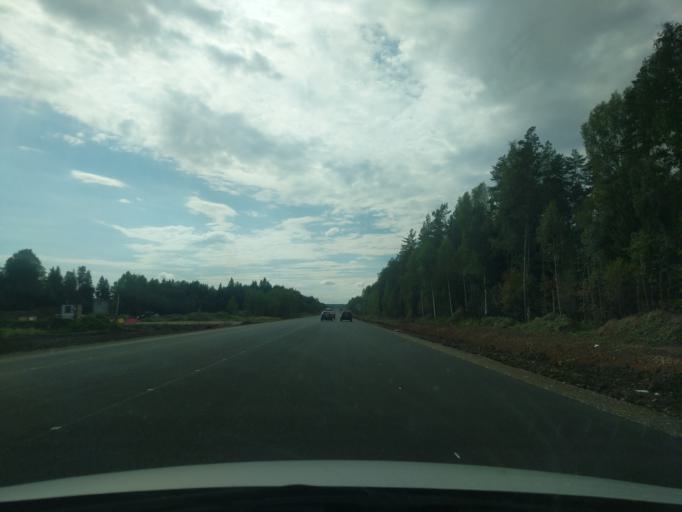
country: RU
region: Kostroma
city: Sudislavl'
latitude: 57.8221
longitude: 41.4929
